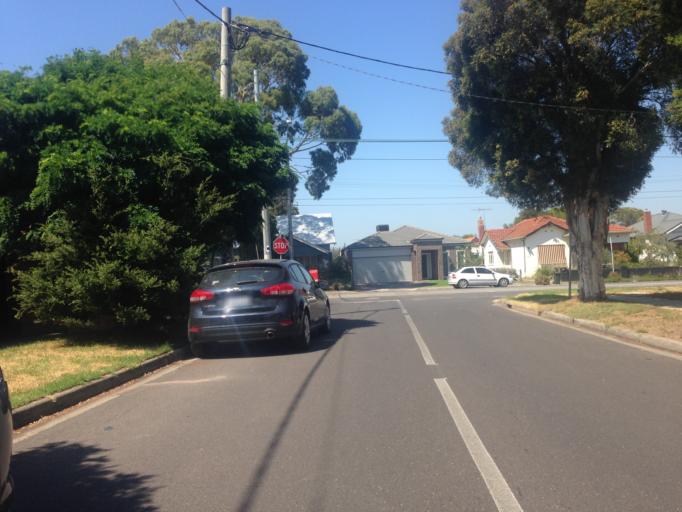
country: AU
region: Victoria
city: Thornbury
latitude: -37.7513
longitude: 144.9941
